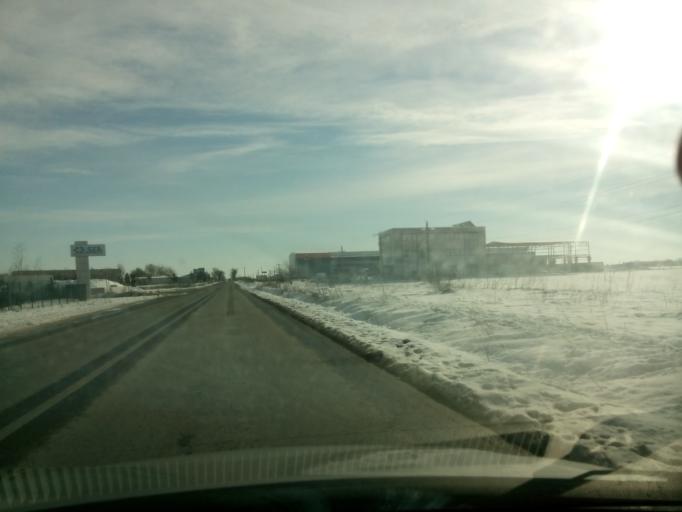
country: RO
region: Ilfov
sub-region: Comuna Popesti-Leordeni
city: Popesti-Leordeni
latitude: 44.3660
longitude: 26.1889
